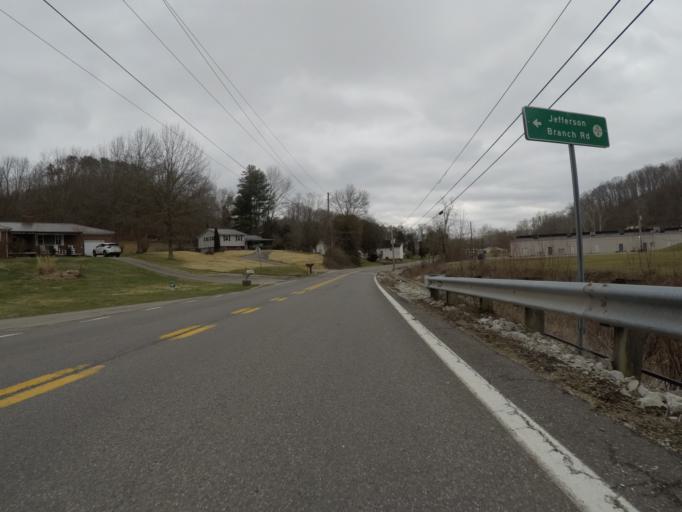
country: US
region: West Virginia
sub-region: Cabell County
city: Barboursville
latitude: 38.4281
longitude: -82.2919
